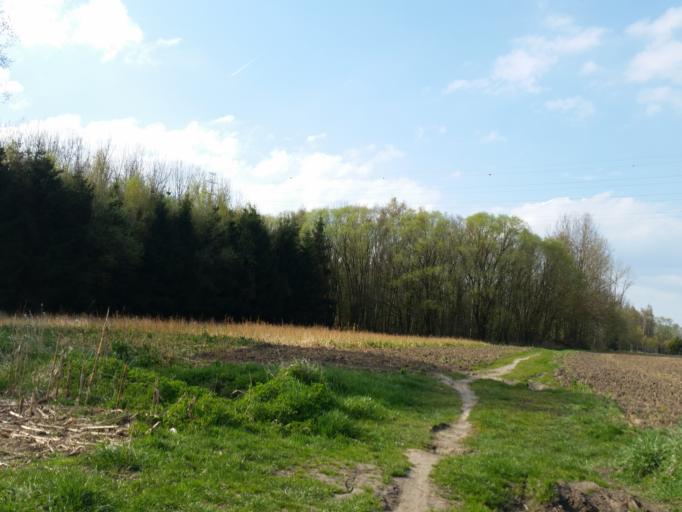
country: BE
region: Flanders
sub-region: Provincie Vlaams-Brabant
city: Kampenhout
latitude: 50.9570
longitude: 4.5169
